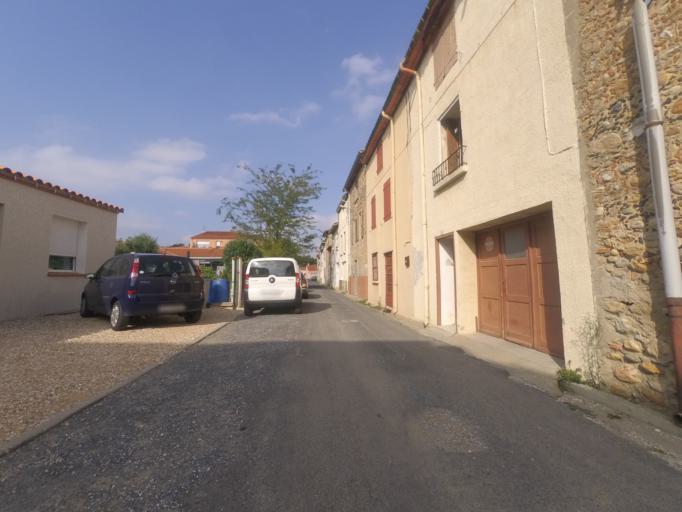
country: FR
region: Languedoc-Roussillon
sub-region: Departement des Pyrenees-Orientales
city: Corneilla-la-Riviere
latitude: 42.6988
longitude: 2.7292
